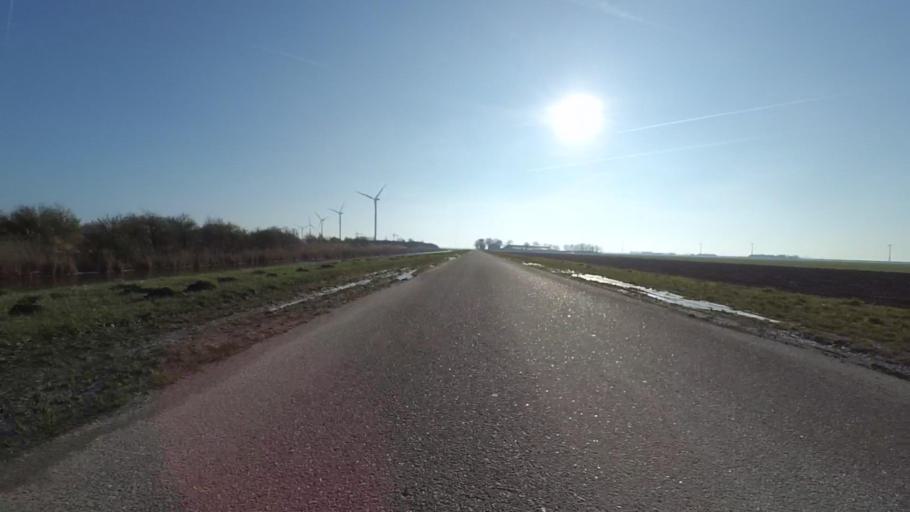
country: NL
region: Utrecht
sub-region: Gemeente Bunschoten
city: Spakenburg
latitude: 52.3075
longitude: 5.3556
